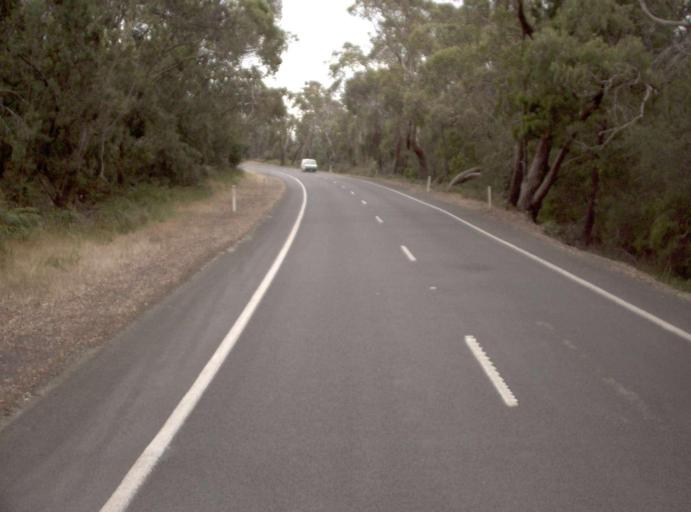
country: AU
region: Victoria
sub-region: Wellington
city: Sale
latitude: -38.2482
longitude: 147.0552
